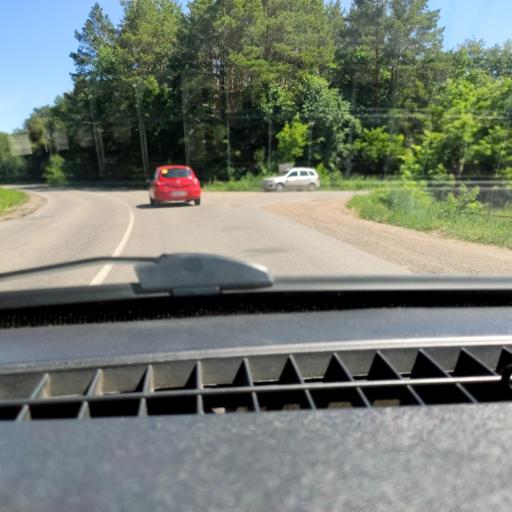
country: RU
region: Bashkortostan
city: Ufa
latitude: 54.5633
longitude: 55.9517
